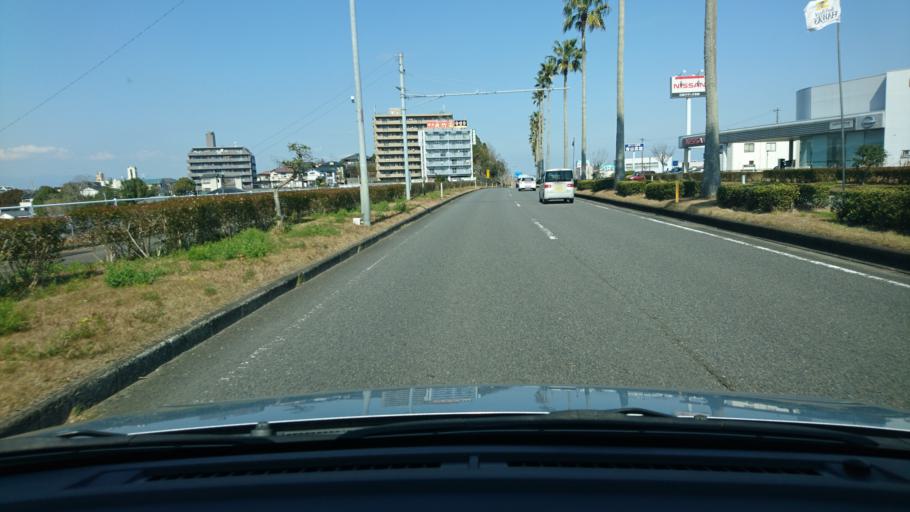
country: JP
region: Miyazaki
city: Miyazaki-shi
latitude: 31.8823
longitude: 131.4109
